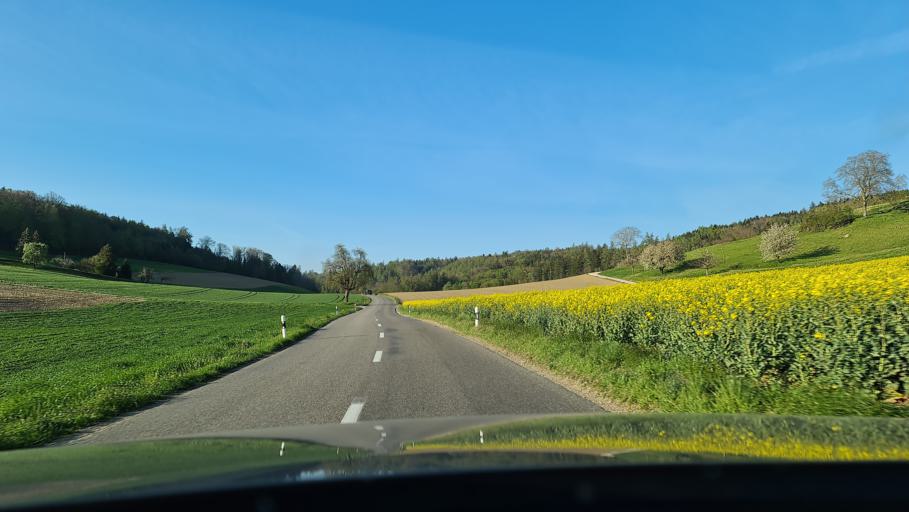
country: CH
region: Aargau
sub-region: Bezirk Lenzburg
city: Egliswil
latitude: 47.3515
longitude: 8.1932
